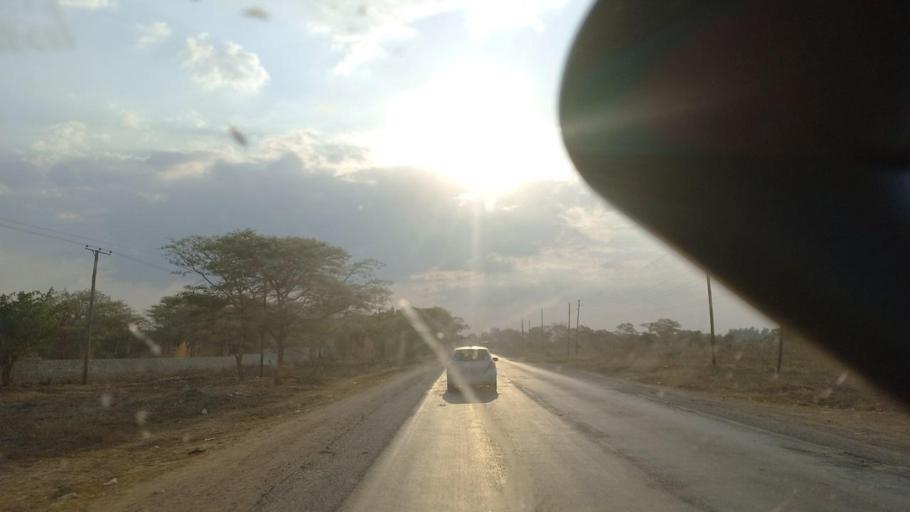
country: ZM
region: Lusaka
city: Lusaka
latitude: -15.3677
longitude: 28.4153
